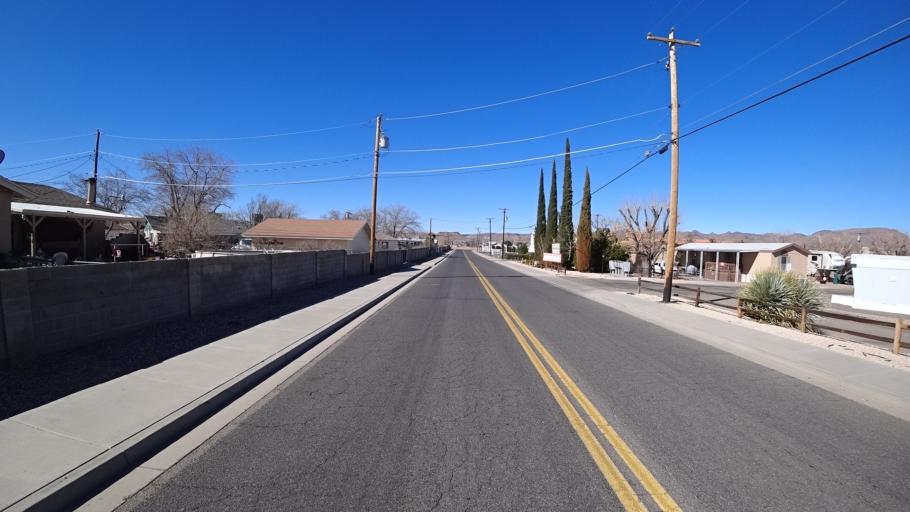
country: US
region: Arizona
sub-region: Mohave County
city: Kingman
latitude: 35.2139
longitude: -114.0218
